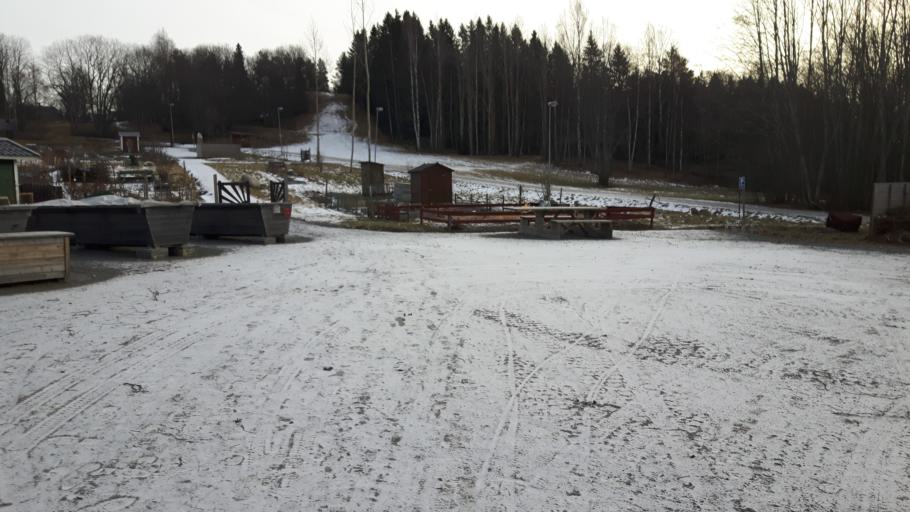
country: SE
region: Vaesternorrland
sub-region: Haernoesands Kommun
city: Haernoesand
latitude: 62.6309
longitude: 17.9658
